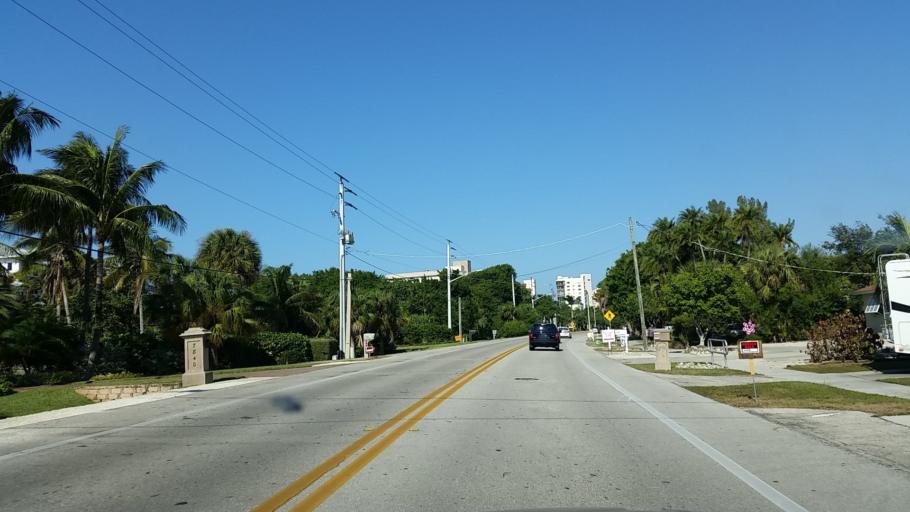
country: US
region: Florida
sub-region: Lee County
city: Fort Myers Beach
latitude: 26.4059
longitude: -81.8947
